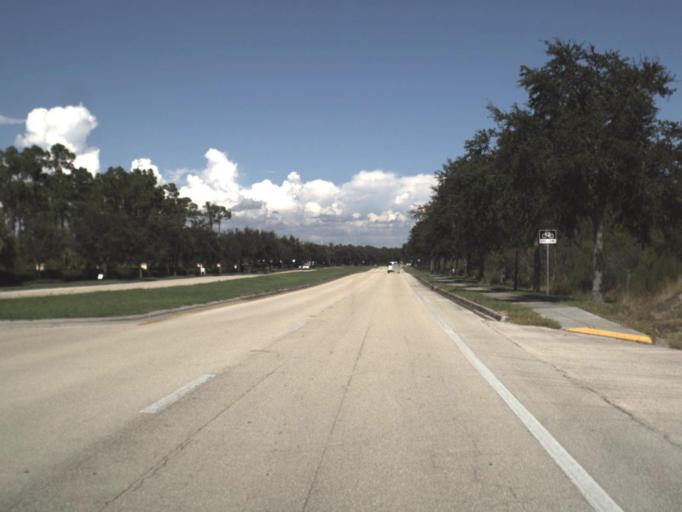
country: US
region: Florida
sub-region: Lee County
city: Palmona Park
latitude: 26.7169
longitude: -81.9212
